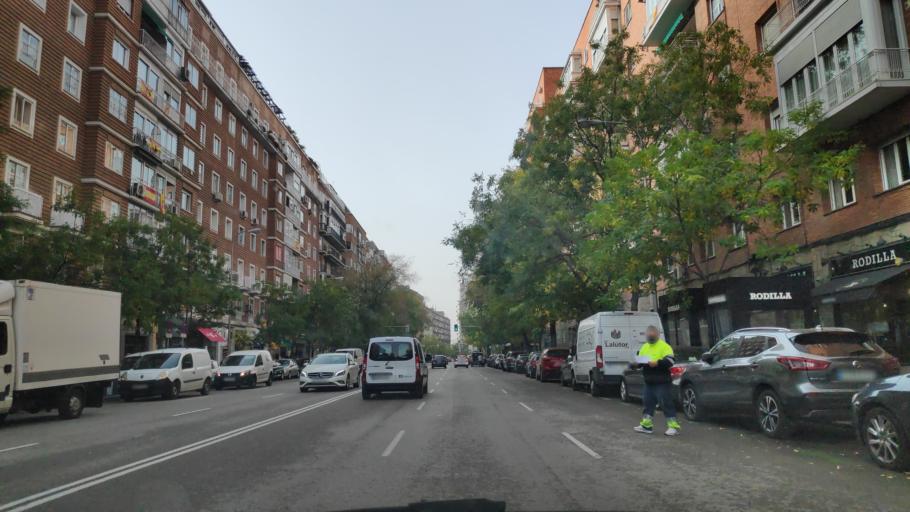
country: ES
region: Madrid
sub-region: Provincia de Madrid
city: Chamartin
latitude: 40.4512
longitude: -3.6866
